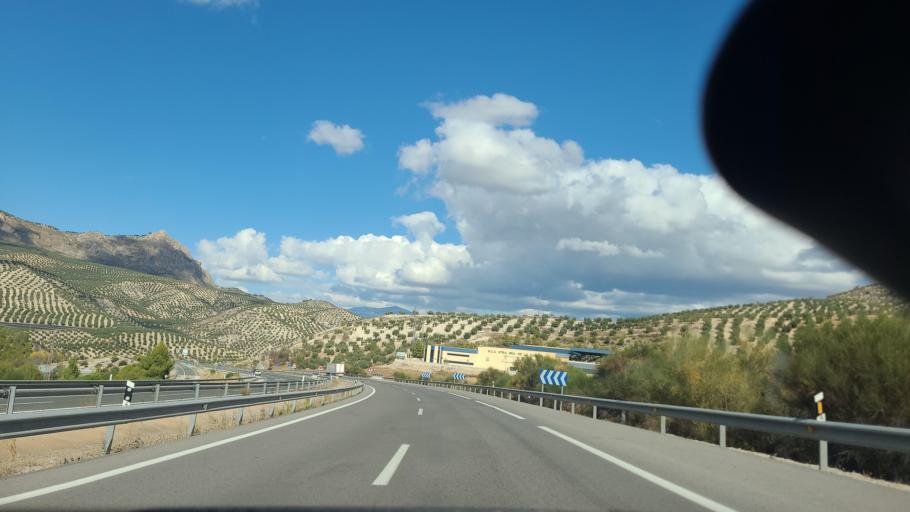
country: ES
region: Andalusia
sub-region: Provincia de Jaen
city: Campillo de Arenas
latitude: 37.5561
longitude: -3.6266
